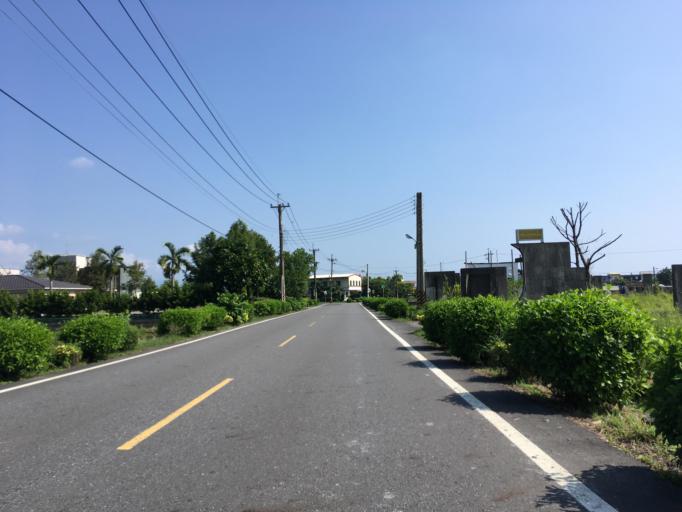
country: TW
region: Taiwan
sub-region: Yilan
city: Yilan
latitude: 24.6780
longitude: 121.7344
